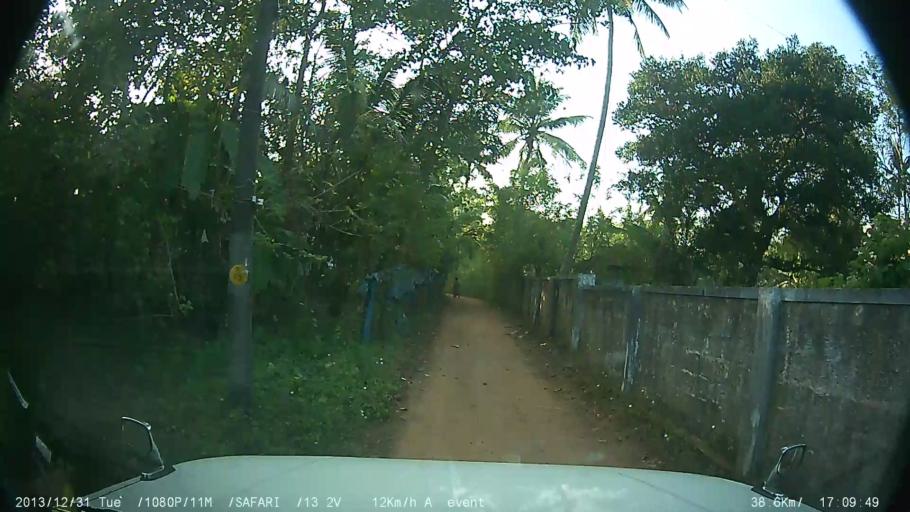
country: IN
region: Kerala
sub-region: Alappuzha
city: Shertallai
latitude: 9.6586
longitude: 76.3784
